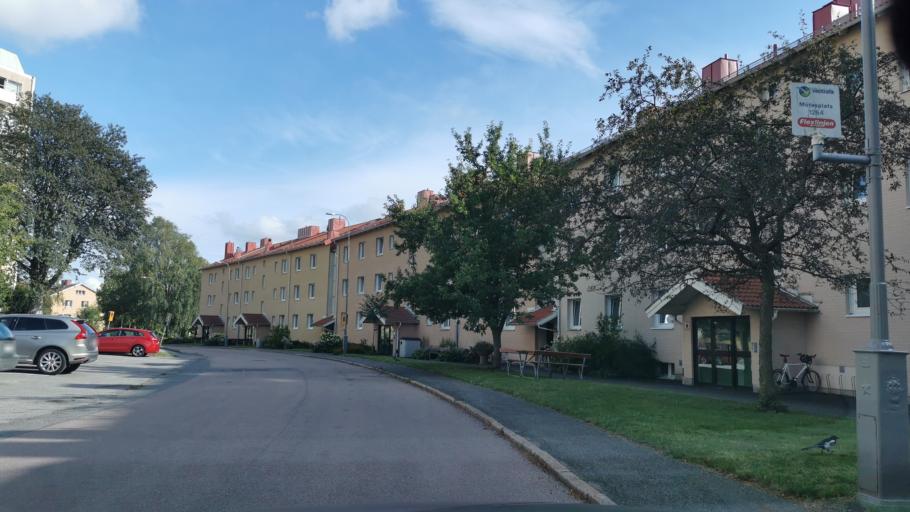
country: SE
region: Vaestra Goetaland
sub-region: Goteborg
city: Majorna
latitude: 57.6575
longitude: 11.9233
